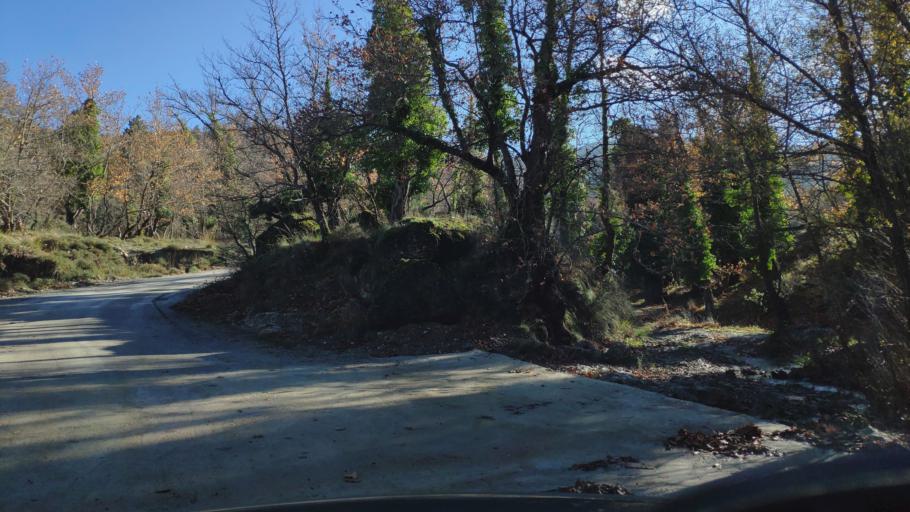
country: GR
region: West Greece
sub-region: Nomos Achaias
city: Aiyira
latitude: 38.0452
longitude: 22.4509
